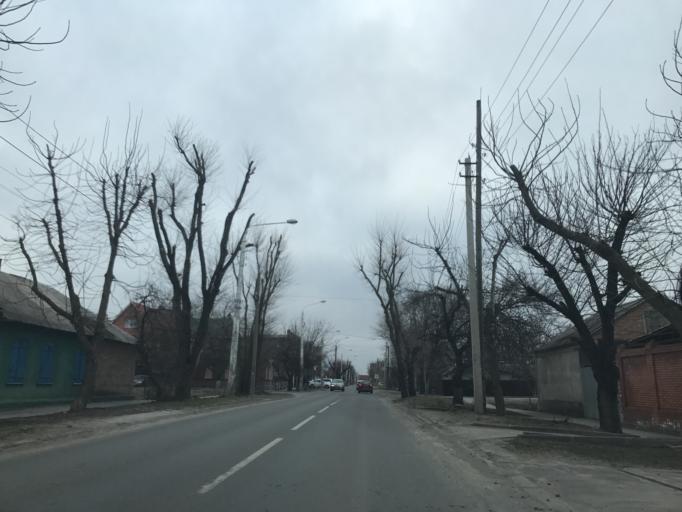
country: RU
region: Rostov
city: Rostov-na-Donu
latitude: 47.2087
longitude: 39.6633
